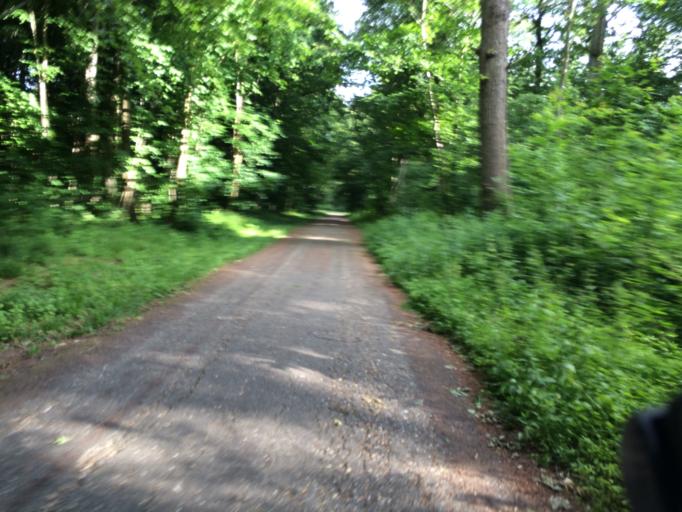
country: FR
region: Ile-de-France
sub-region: Departement de l'Essonne
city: Igny
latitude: 48.7572
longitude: 2.2415
